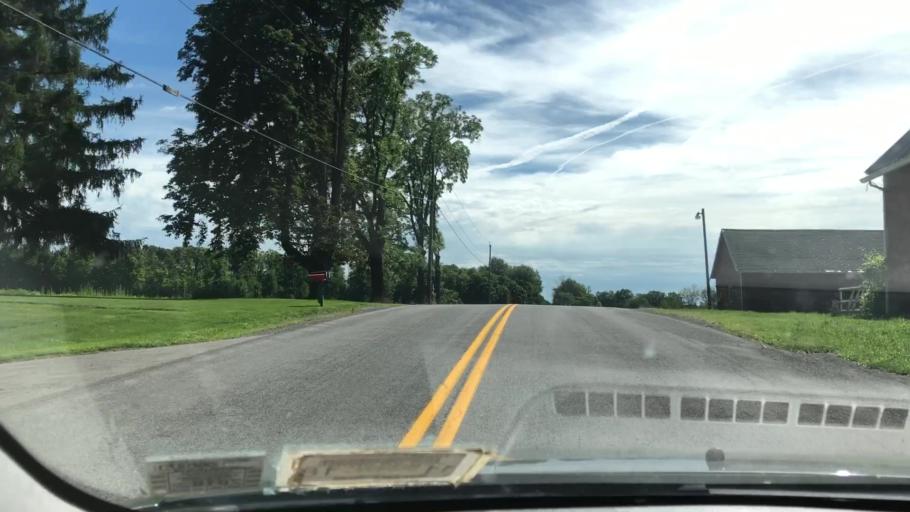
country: US
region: New York
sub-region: Monroe County
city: Fairport
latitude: 43.1282
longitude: -77.3661
